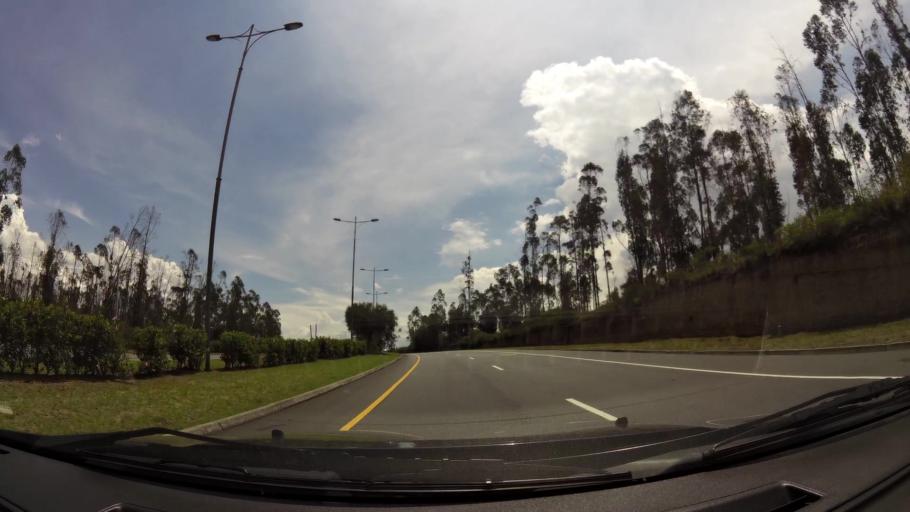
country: EC
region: Pichincha
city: Quito
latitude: -0.1694
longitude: -78.3433
